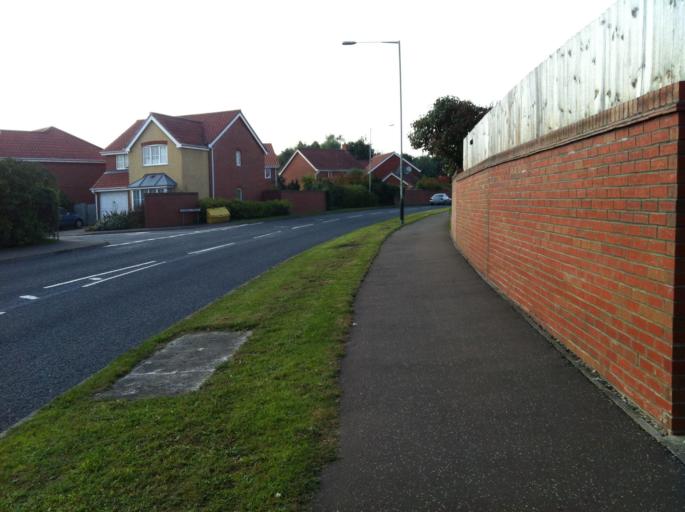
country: GB
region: England
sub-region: Norfolk
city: Bowthorpe
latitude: 52.6291
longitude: 1.2171
